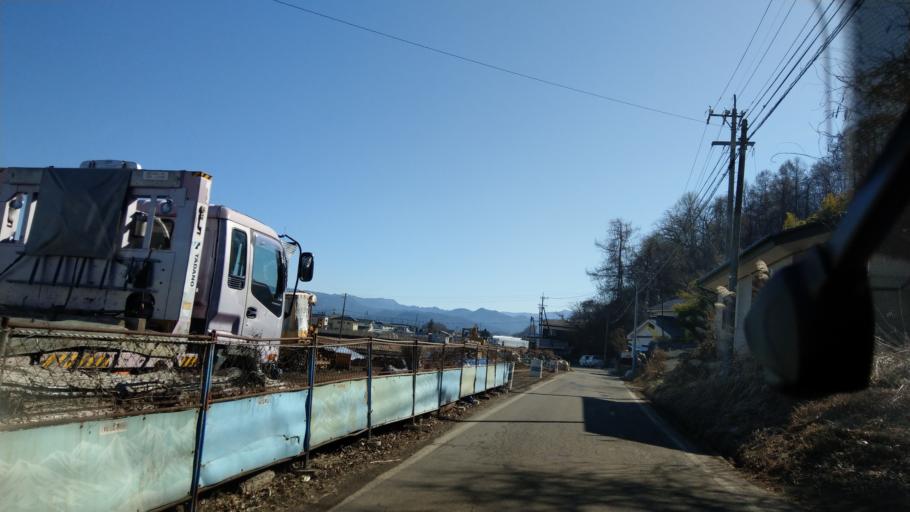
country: JP
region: Nagano
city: Saku
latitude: 36.2204
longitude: 138.4475
